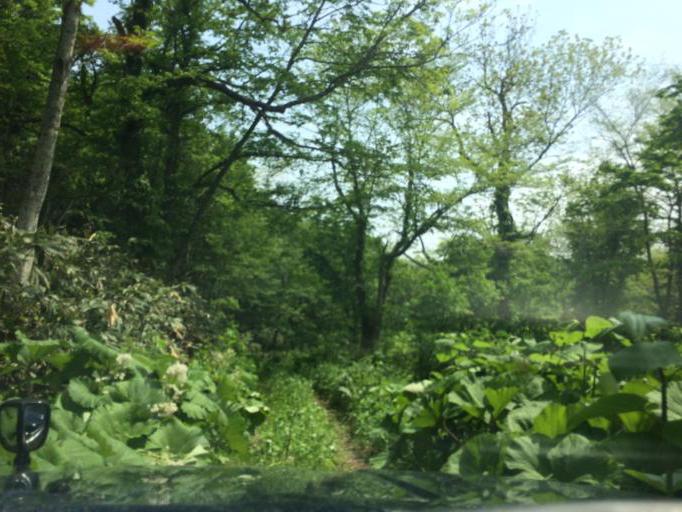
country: JP
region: Hokkaido
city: Niseko Town
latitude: 42.7172
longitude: 140.5506
